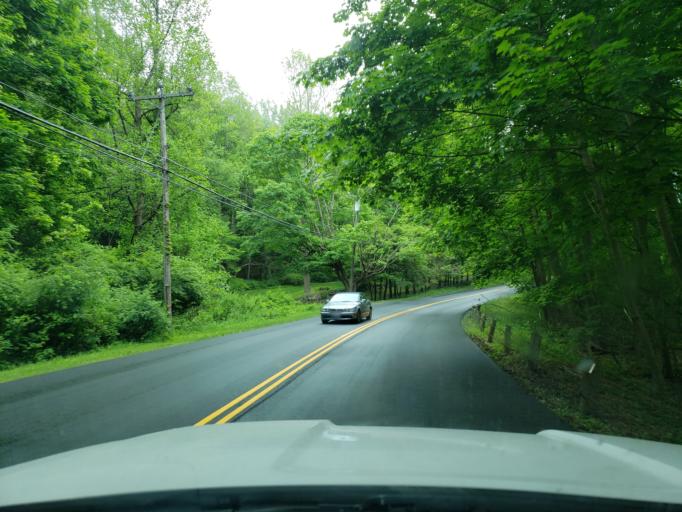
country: US
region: Connecticut
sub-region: Fairfield County
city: Ridgefield
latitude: 41.2929
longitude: -73.5258
